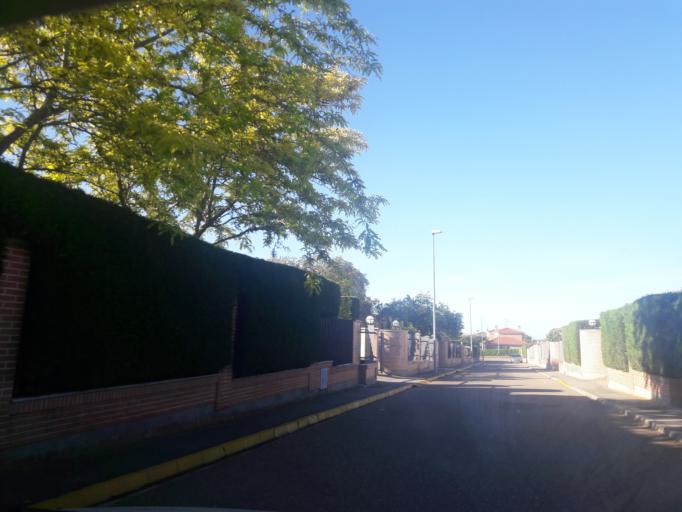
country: ES
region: Castille and Leon
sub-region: Provincia de Salamanca
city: Martinamor
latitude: 40.8091
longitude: -5.6331
